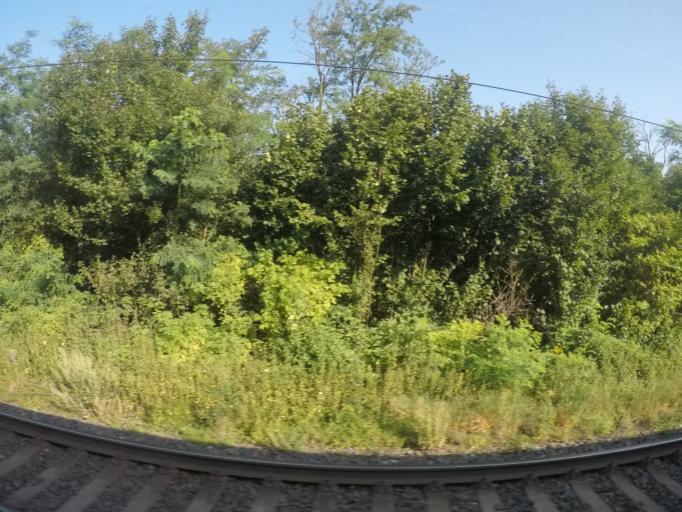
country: SK
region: Presovsky
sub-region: Okres Presov
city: Presov
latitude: 48.8532
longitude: 21.1824
